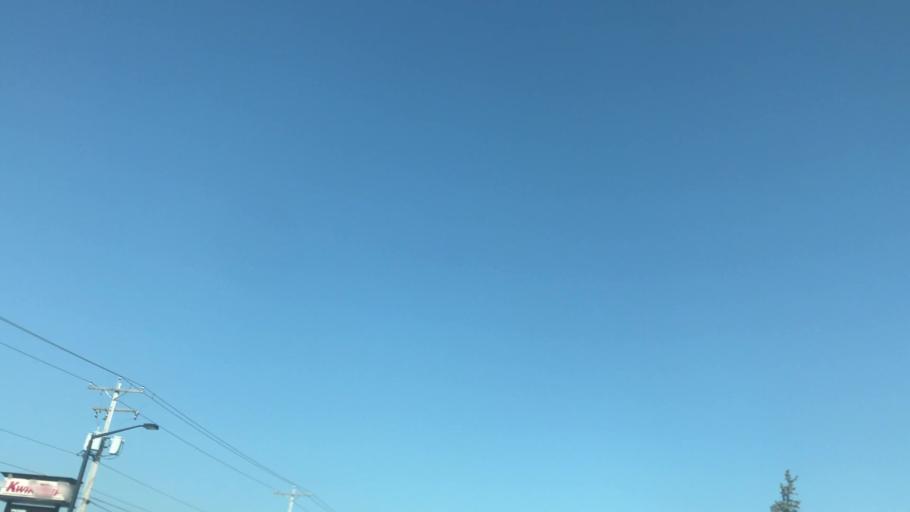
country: US
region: Wisconsin
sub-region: Brown County
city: Ashwaubenon
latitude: 44.4980
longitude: -88.0463
